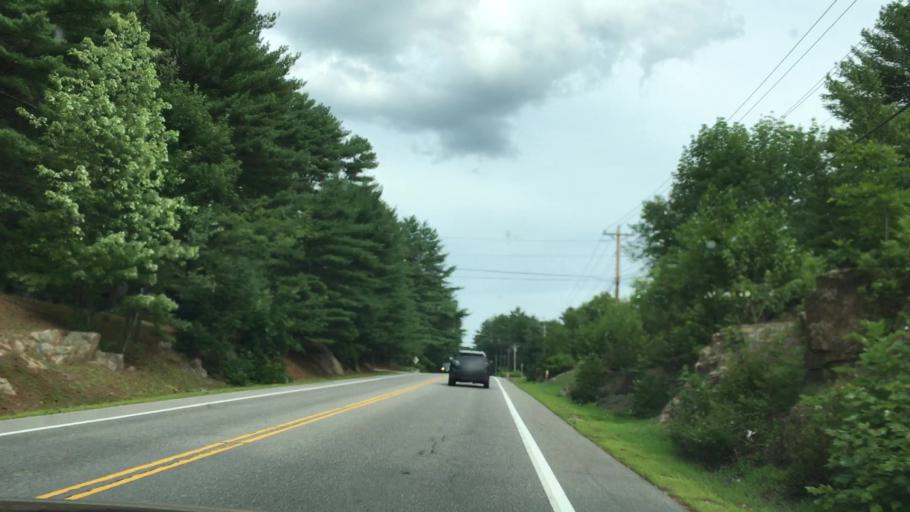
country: US
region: New Hampshire
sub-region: Grafton County
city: Ashland
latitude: 43.6206
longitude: -71.5930
